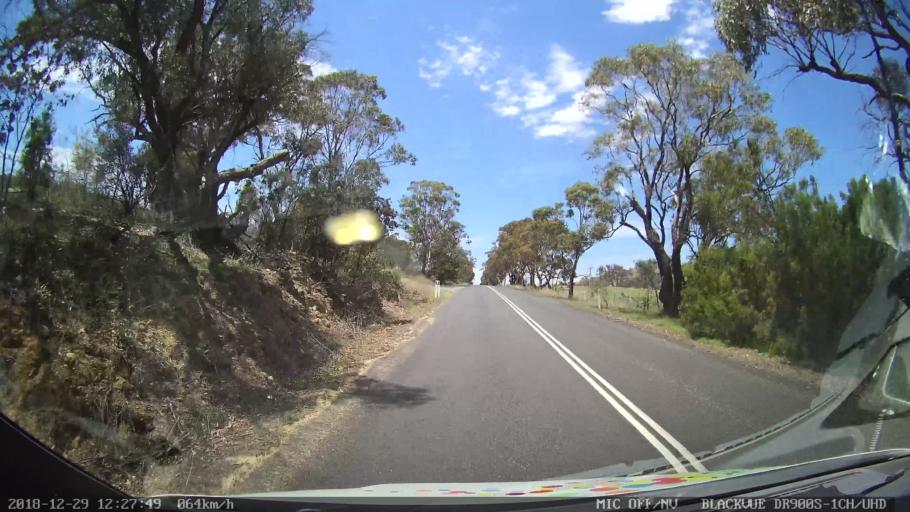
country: AU
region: Australian Capital Territory
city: Macarthur
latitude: -35.4804
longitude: 149.2243
